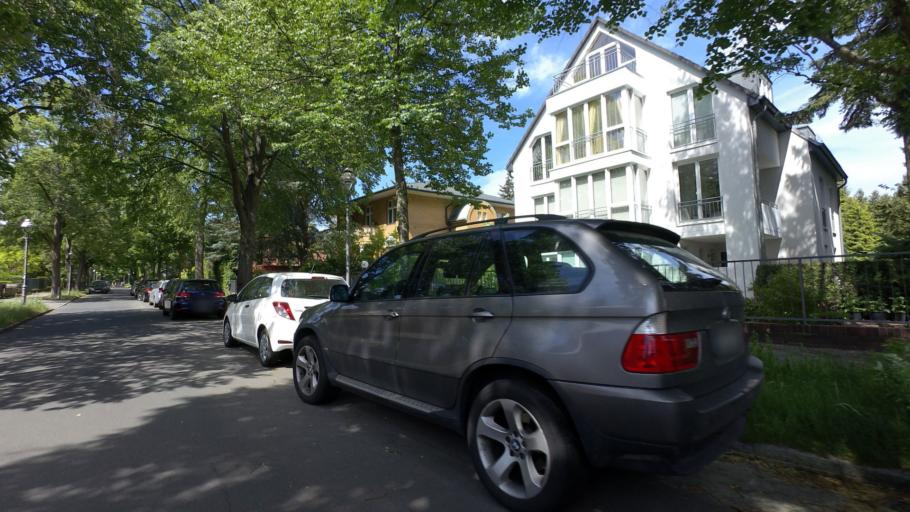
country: DE
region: Berlin
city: Lankwitz
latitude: 52.4172
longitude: 13.3396
